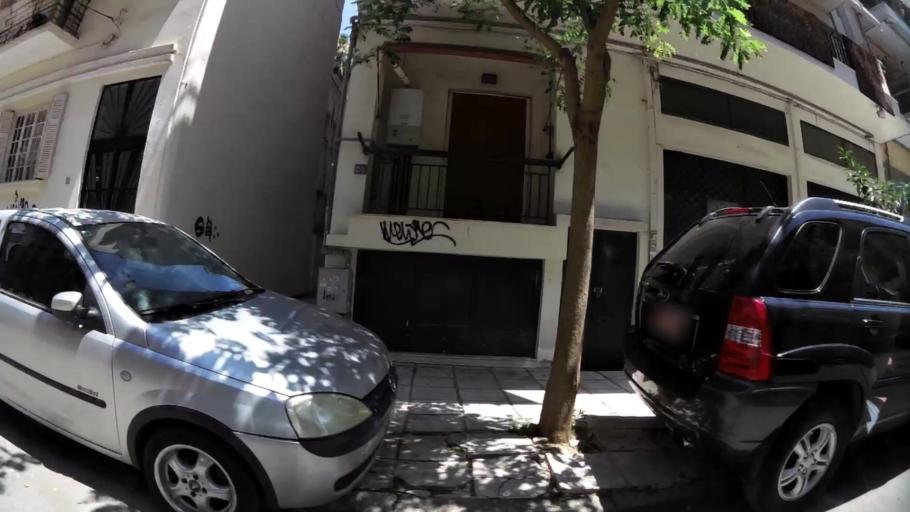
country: GR
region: Central Macedonia
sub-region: Nomos Thessalonikis
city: Triandria
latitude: 40.6116
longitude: 22.9595
